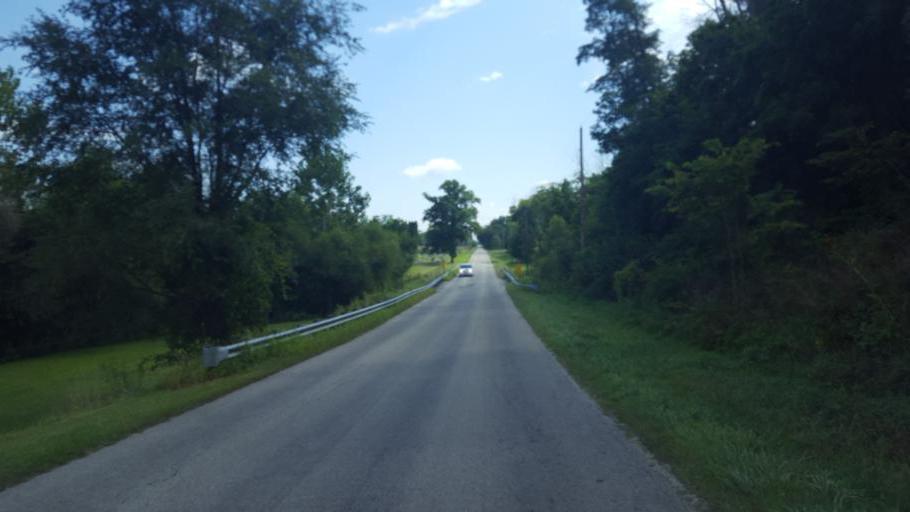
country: US
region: Ohio
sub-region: Seneca County
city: Tiffin
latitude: 41.0661
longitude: -83.0971
